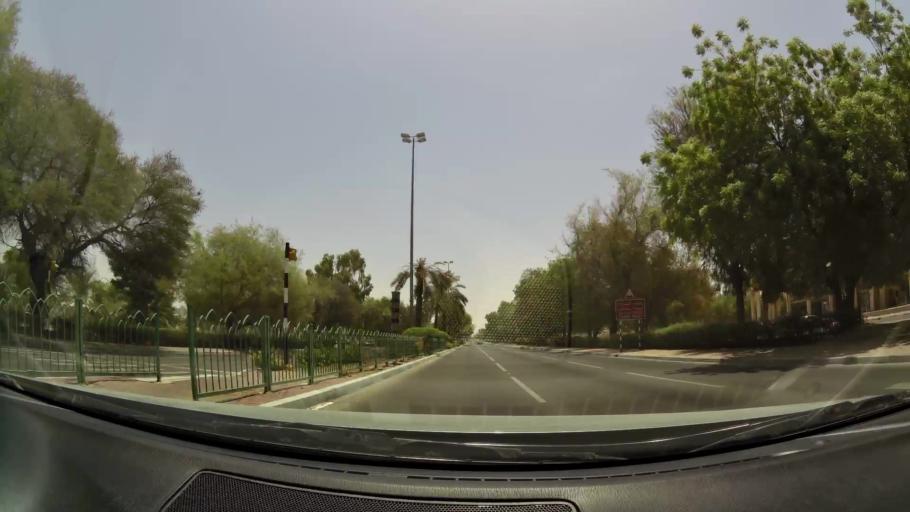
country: OM
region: Al Buraimi
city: Al Buraymi
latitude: 24.2699
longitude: 55.7455
